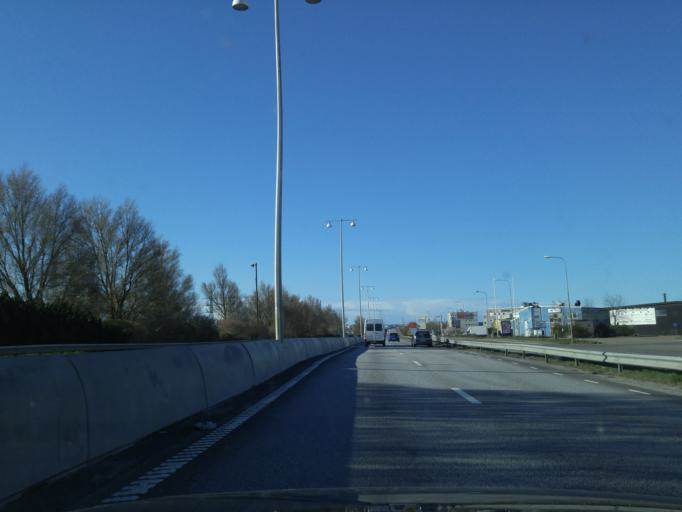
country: SE
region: Vaestra Goetaland
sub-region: Goteborg
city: Goeteborg
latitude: 57.7349
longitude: 12.0021
